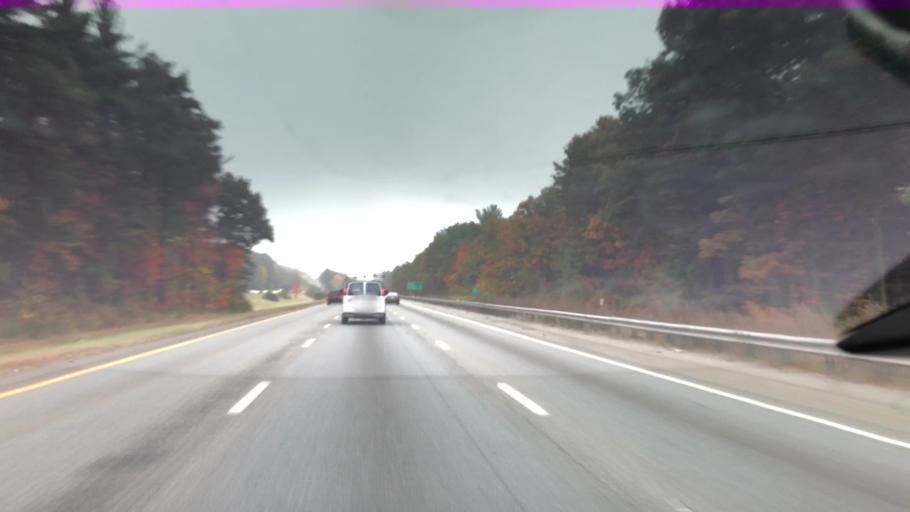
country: US
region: Massachusetts
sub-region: Worcester County
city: Harvard
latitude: 42.4700
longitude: -71.5593
